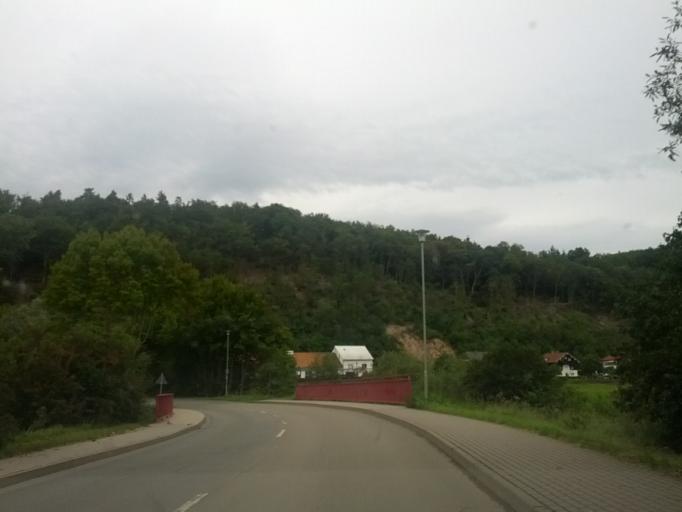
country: DE
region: Thuringia
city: Bad Salzungen
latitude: 50.8183
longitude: 10.2255
